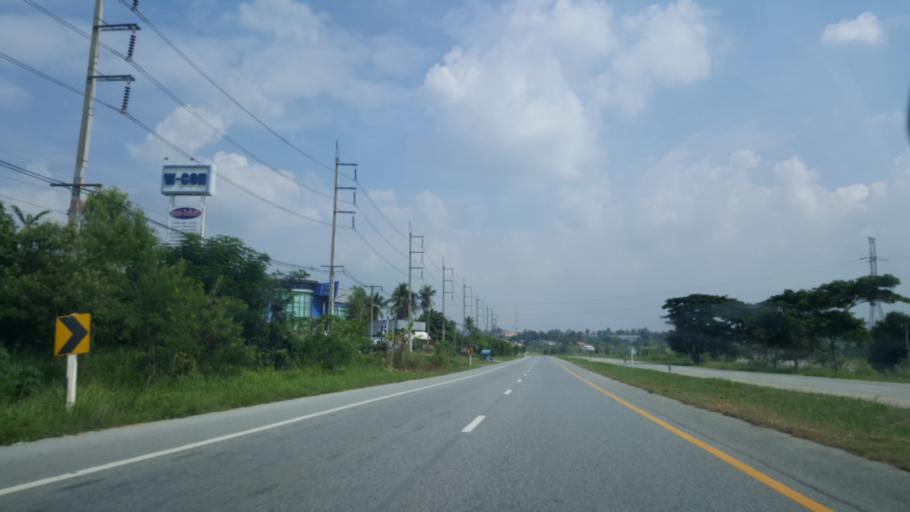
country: TH
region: Chon Buri
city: Ban Talat Bueng
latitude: 12.9355
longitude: 101.0380
